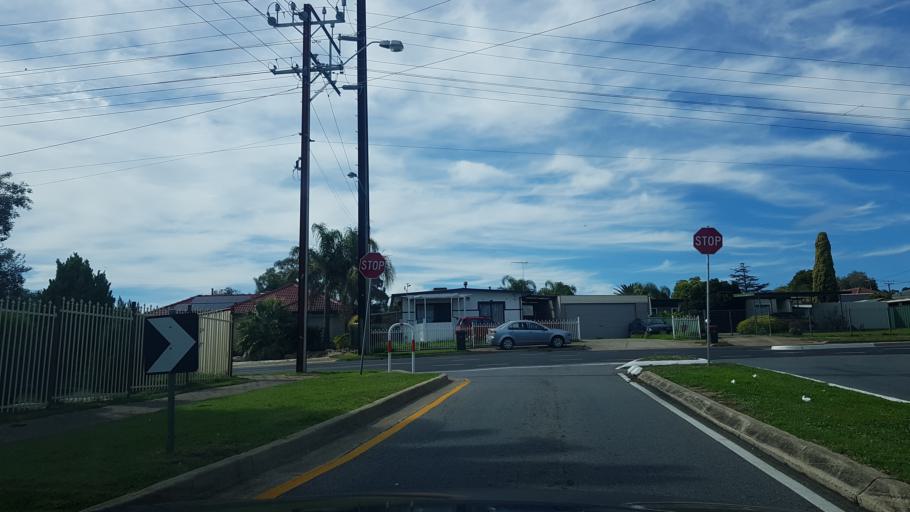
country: AU
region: South Australia
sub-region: Tea Tree Gully
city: Modbury
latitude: -34.8123
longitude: 138.6600
